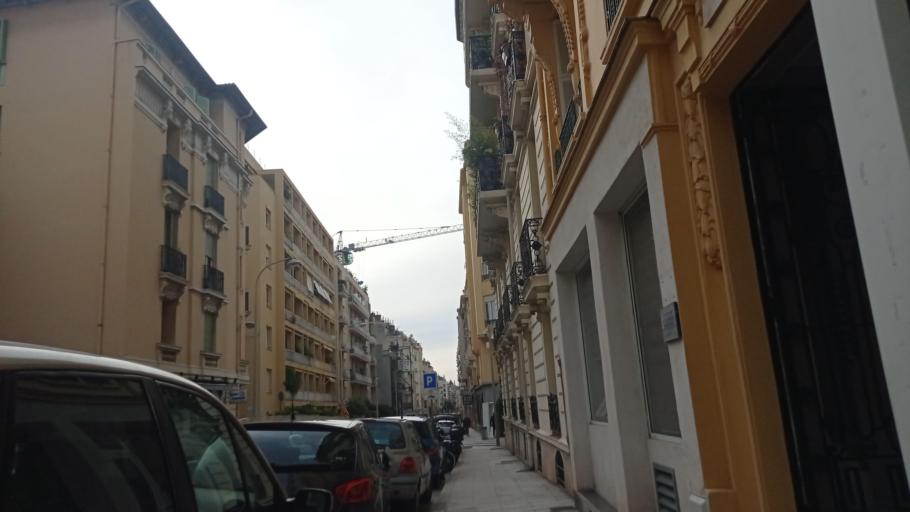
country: FR
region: Provence-Alpes-Cote d'Azur
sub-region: Departement des Alpes-Maritimes
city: Nice
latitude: 43.7024
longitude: 7.2597
